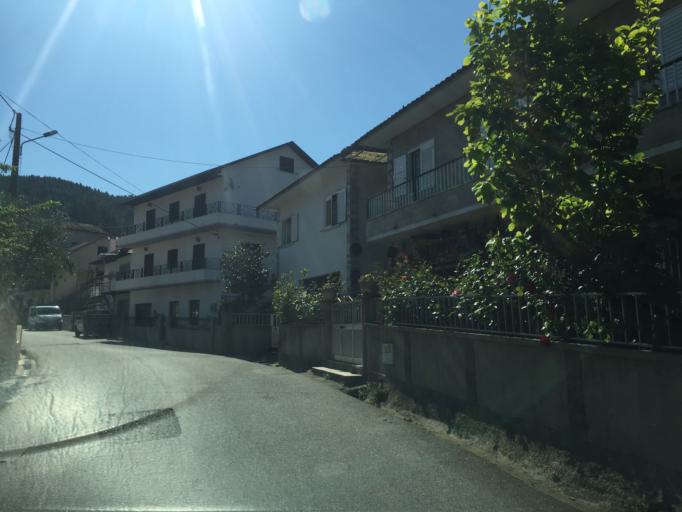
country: PT
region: Coimbra
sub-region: Pampilhosa da Serra
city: Pampilhosa da Serra
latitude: 40.0838
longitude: -7.7870
